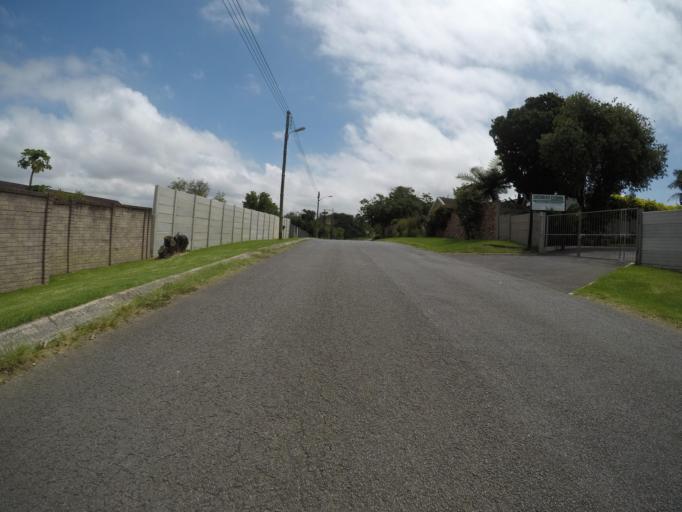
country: ZA
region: Eastern Cape
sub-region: Buffalo City Metropolitan Municipality
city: East London
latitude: -32.9391
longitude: 28.0035
